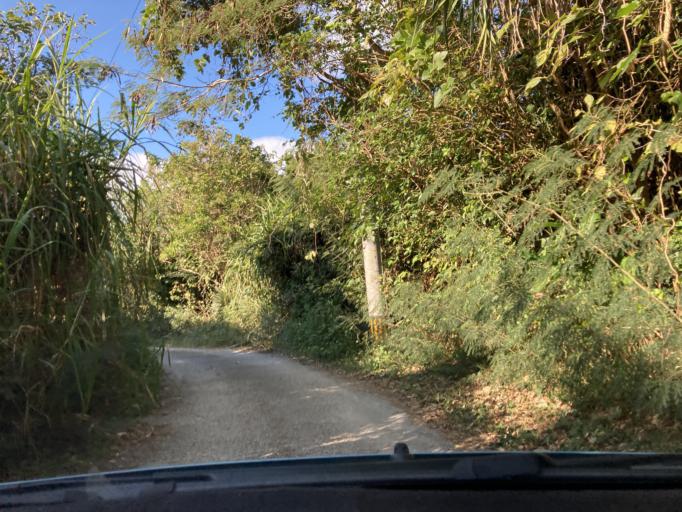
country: JP
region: Okinawa
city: Katsuren-haebaru
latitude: 26.3165
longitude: 127.9280
